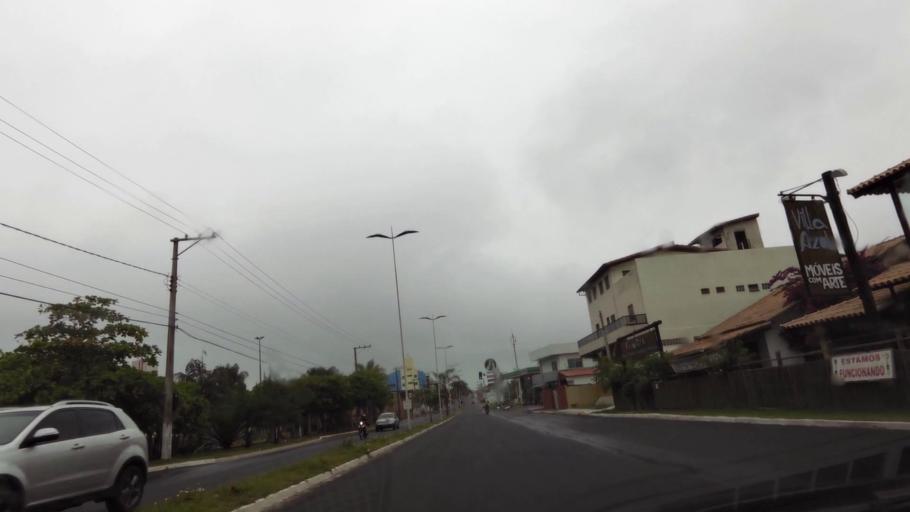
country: BR
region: Espirito Santo
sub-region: Guarapari
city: Guarapari
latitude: -20.7234
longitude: -40.5255
